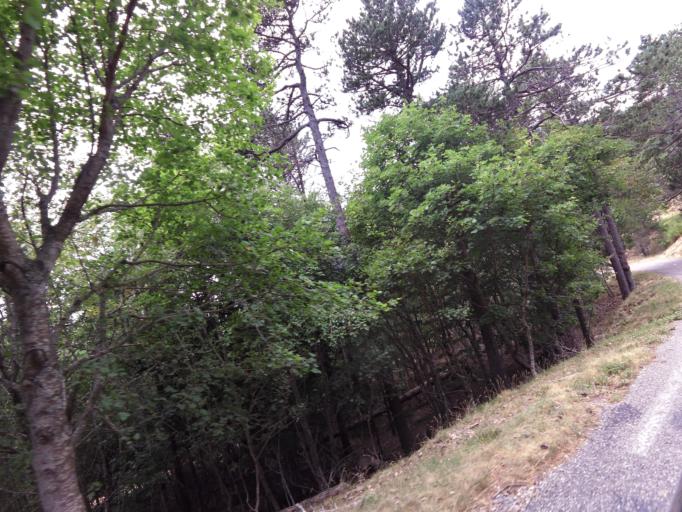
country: FR
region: Languedoc-Roussillon
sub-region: Departement du Gard
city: Valleraugue
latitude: 44.0482
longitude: 3.6090
